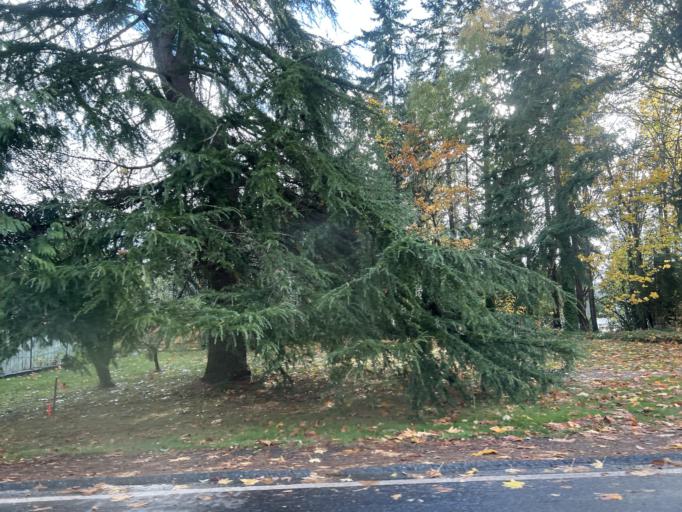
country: US
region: Washington
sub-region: Kitsap County
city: Bainbridge Island
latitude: 47.6285
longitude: -122.5174
